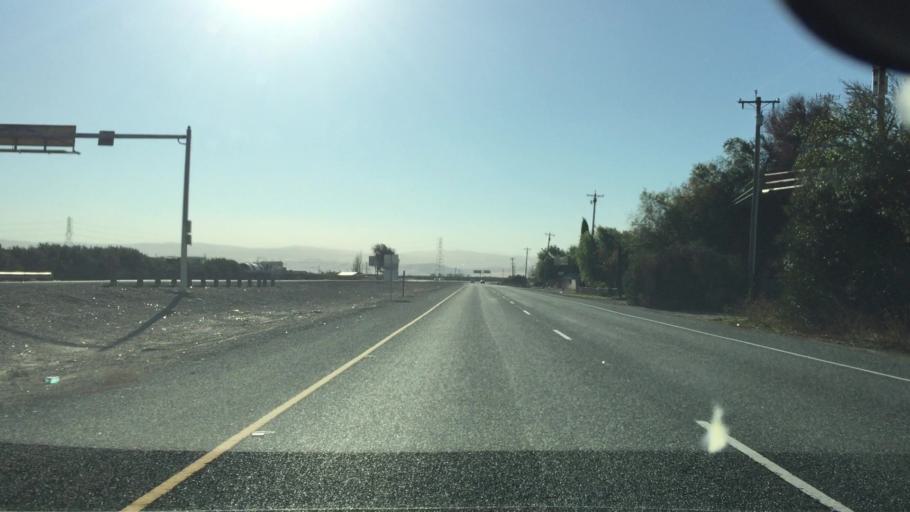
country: US
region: California
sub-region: San Joaquin County
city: Tracy
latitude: 37.7436
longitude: -121.3649
